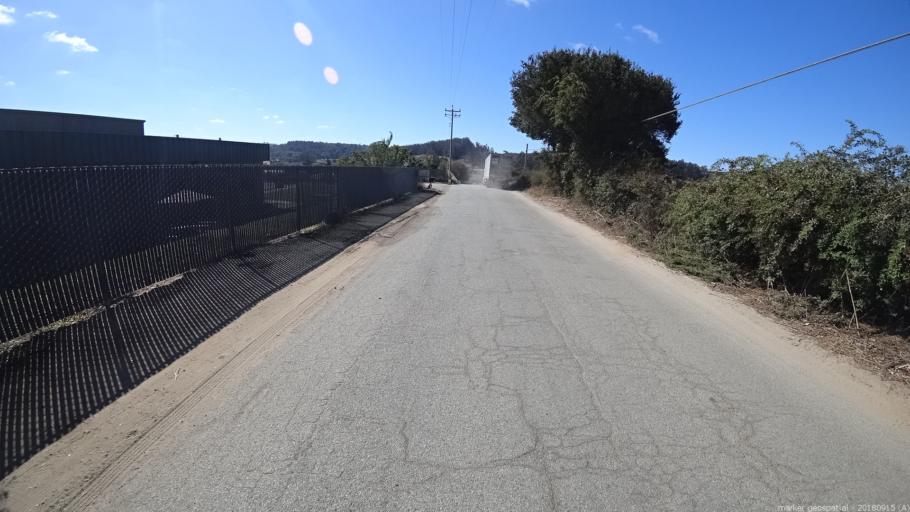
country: US
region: California
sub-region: Monterey County
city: Las Lomas
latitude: 36.8675
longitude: -121.7225
